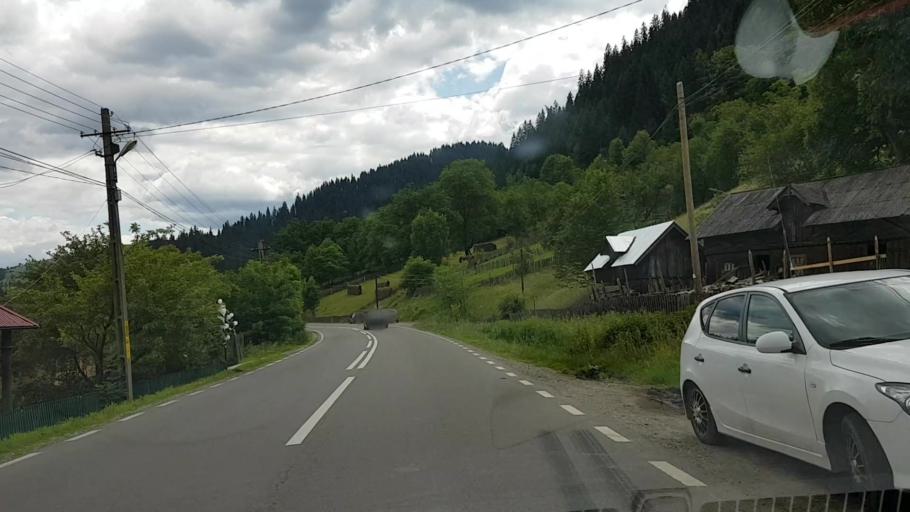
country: RO
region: Neamt
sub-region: Comuna Borca
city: Borca
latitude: 47.1862
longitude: 25.7742
